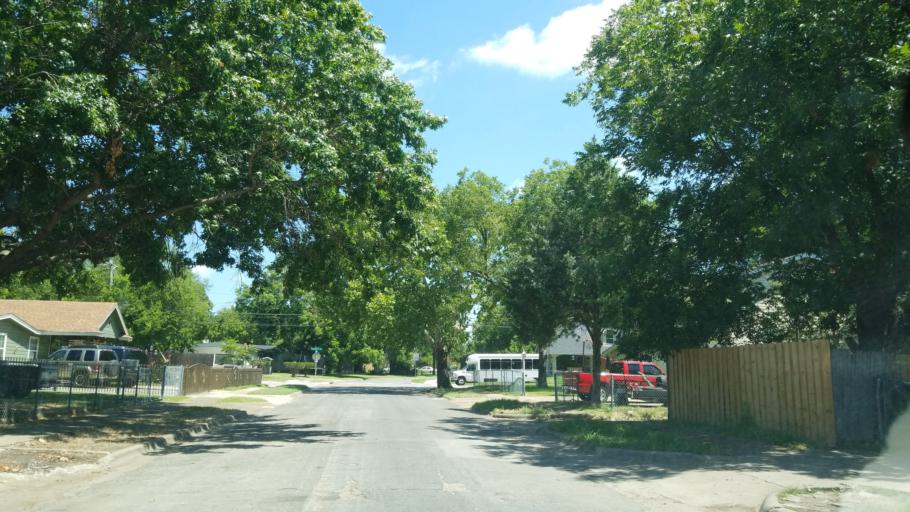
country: US
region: Texas
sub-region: Dallas County
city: Balch Springs
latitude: 32.7410
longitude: -96.6955
